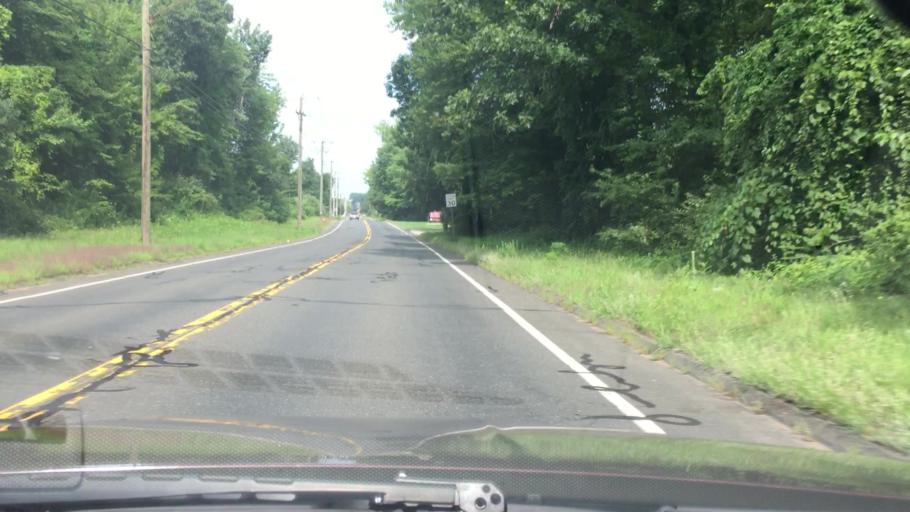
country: US
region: Connecticut
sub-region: Hartford County
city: South Windsor
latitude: 41.8291
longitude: -72.5933
